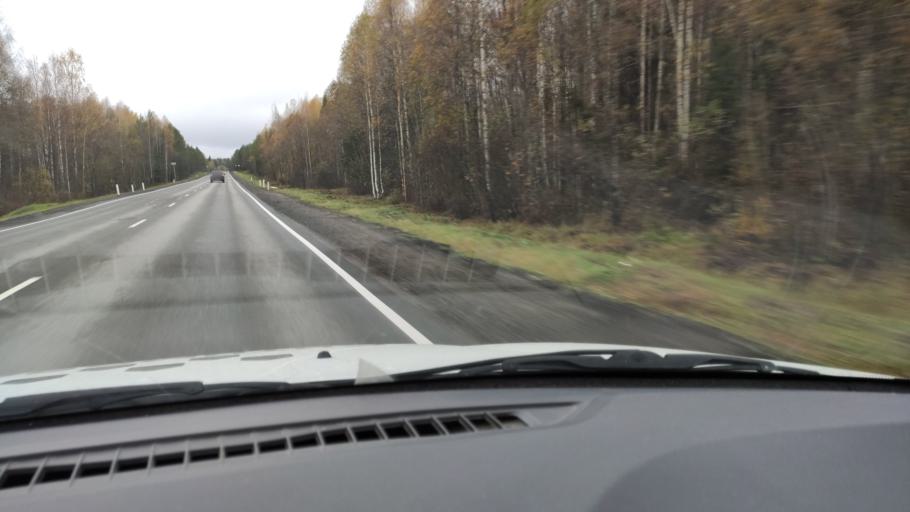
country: RU
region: Kirov
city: Belaya Kholunitsa
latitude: 58.8996
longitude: 50.9282
